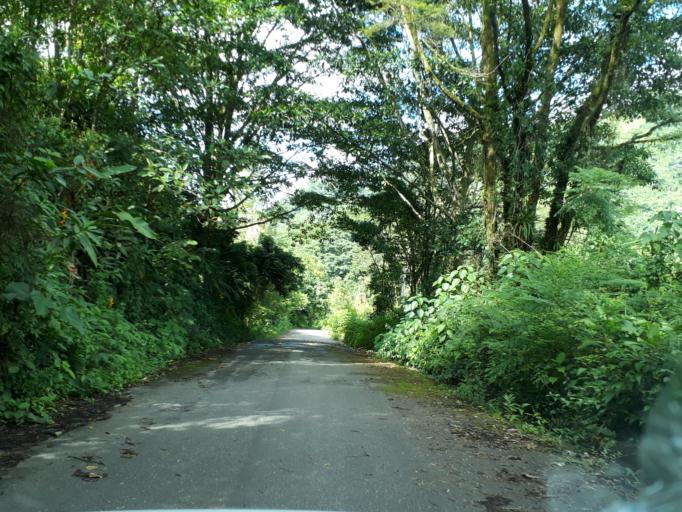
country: CO
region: Boyaca
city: Santa Maria
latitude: 4.7428
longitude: -73.3389
